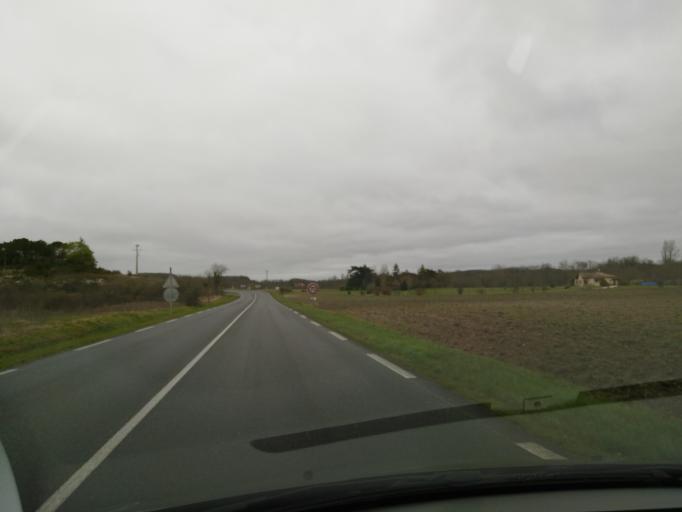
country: FR
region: Aquitaine
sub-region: Departement du Lot-et-Garonne
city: Castillonnes
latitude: 44.7179
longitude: 0.5579
